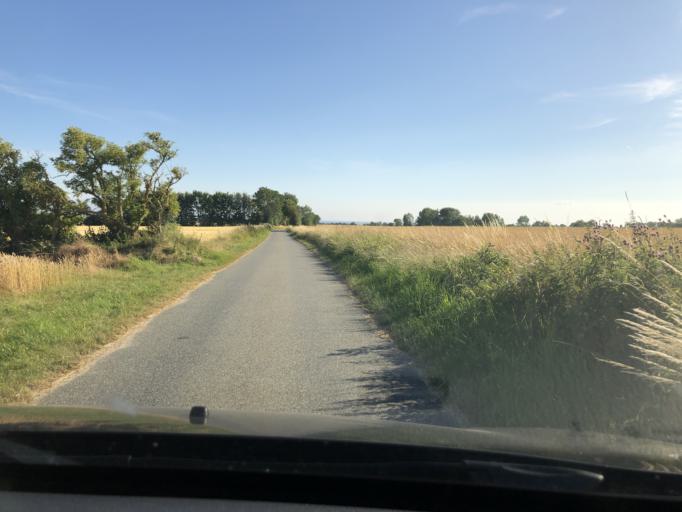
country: DK
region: South Denmark
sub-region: AEro Kommune
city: AEroskobing
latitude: 54.8582
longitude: 10.3800
